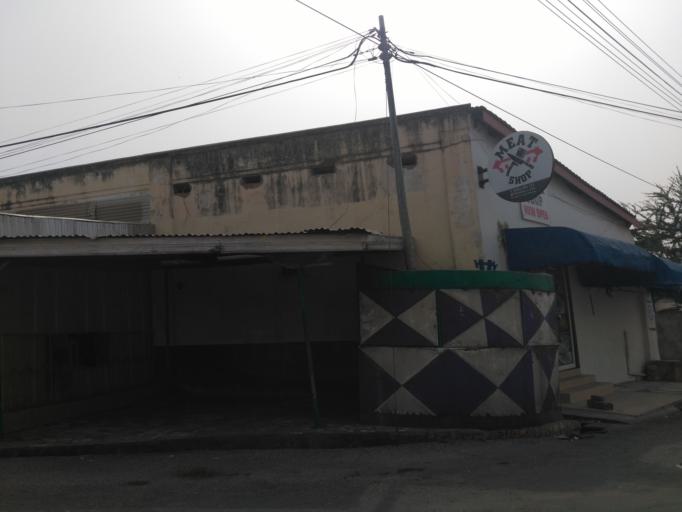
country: GH
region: Ashanti
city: Kumasi
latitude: 6.6895
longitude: -1.6244
